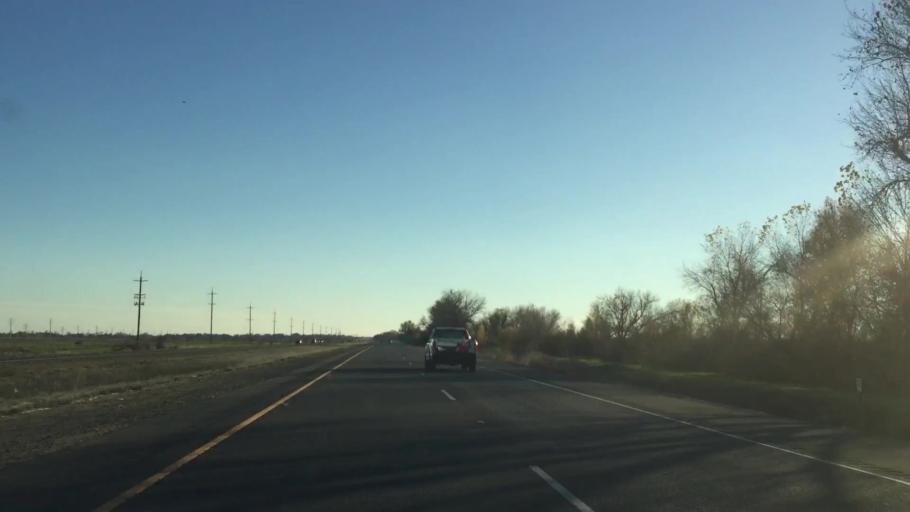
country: US
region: California
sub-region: Yuba County
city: Plumas Lake
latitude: 39.0005
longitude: -121.5435
